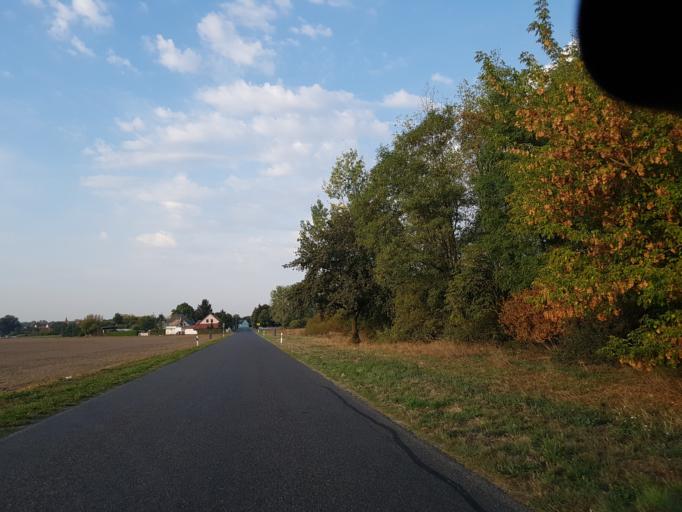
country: DE
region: Brandenburg
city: Hohenleipisch
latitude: 51.4731
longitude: 13.5707
